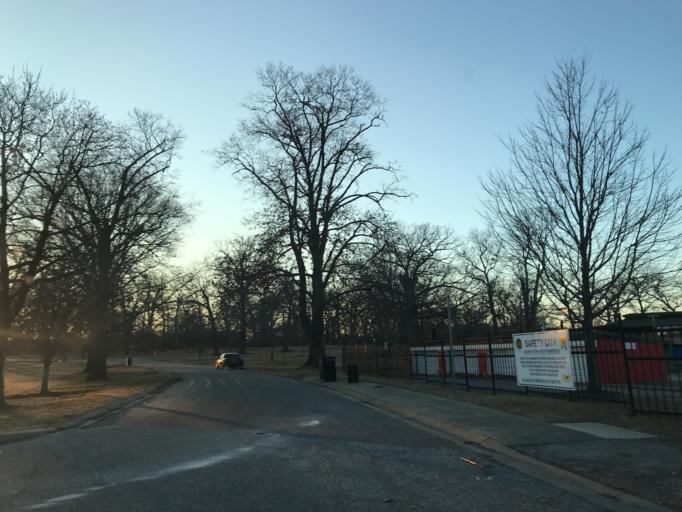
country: US
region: Maryland
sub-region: City of Baltimore
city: Baltimore
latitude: 39.3214
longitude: -76.6380
